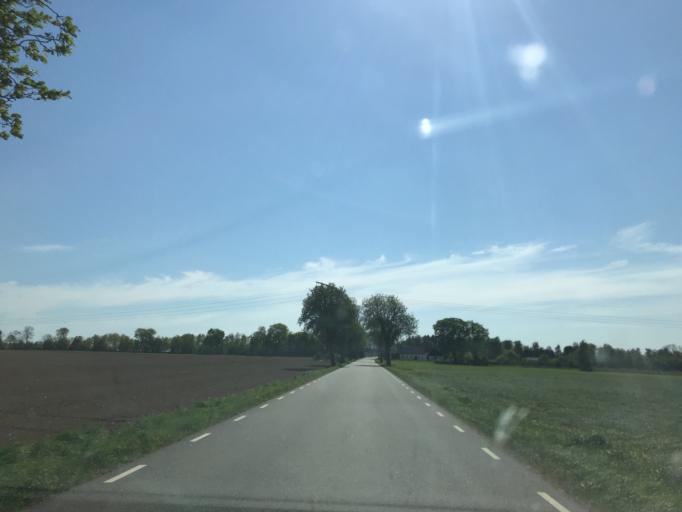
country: SE
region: Skane
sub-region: Svalovs Kommun
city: Svaloev
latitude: 55.9422
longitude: 13.0268
